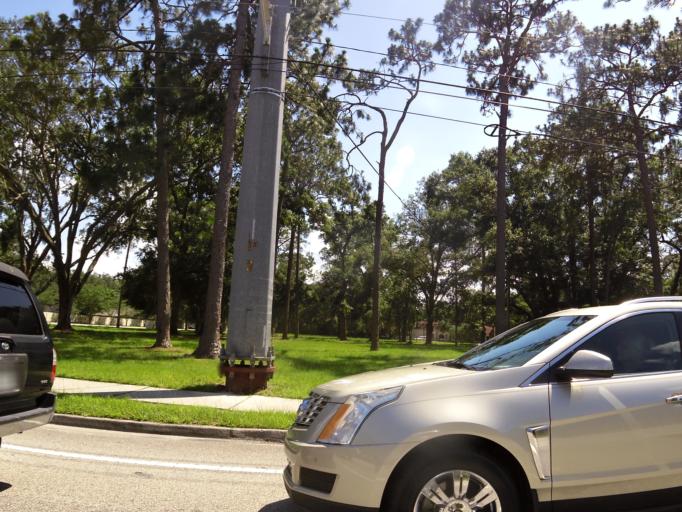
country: US
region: Florida
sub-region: Saint Johns County
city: Fruit Cove
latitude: 30.1590
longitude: -81.5979
